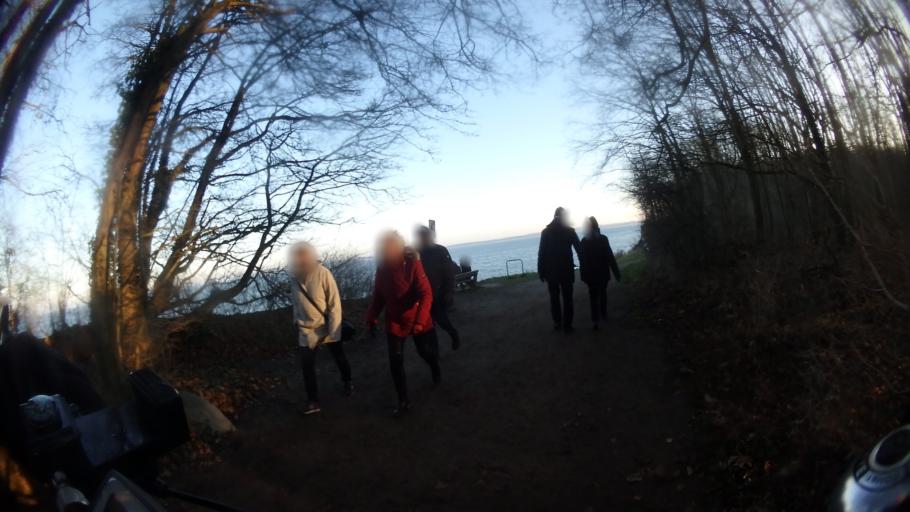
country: DE
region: Schleswig-Holstein
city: Travemuende
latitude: 53.9855
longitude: 10.8779
